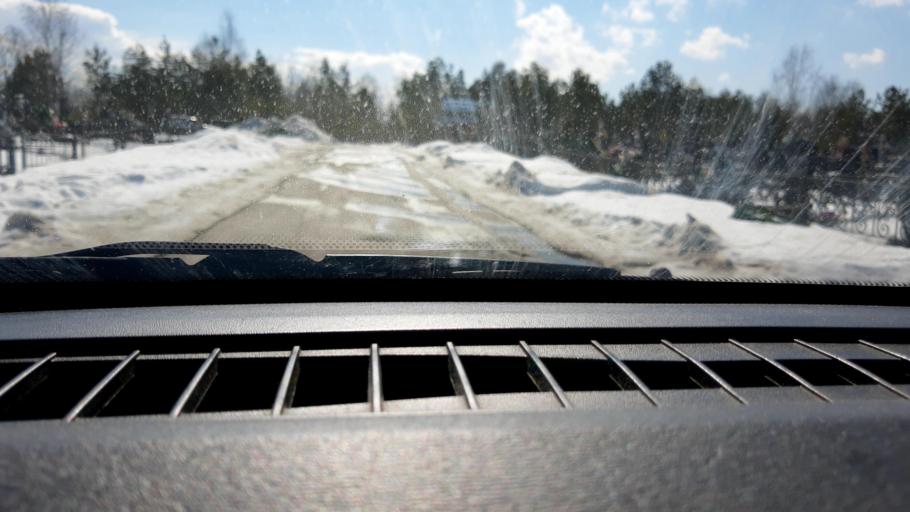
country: RU
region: Nizjnij Novgorod
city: Gorbatovka
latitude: 56.3610
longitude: 43.7676
